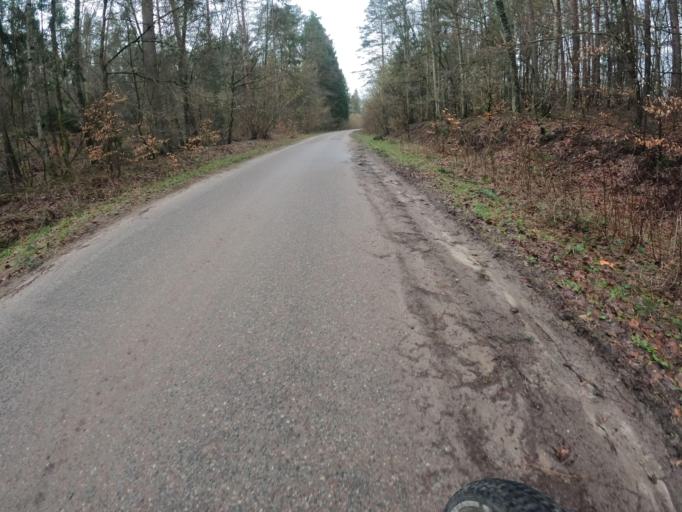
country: PL
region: West Pomeranian Voivodeship
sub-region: Powiat slawienski
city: Slawno
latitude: 54.2584
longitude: 16.6606
